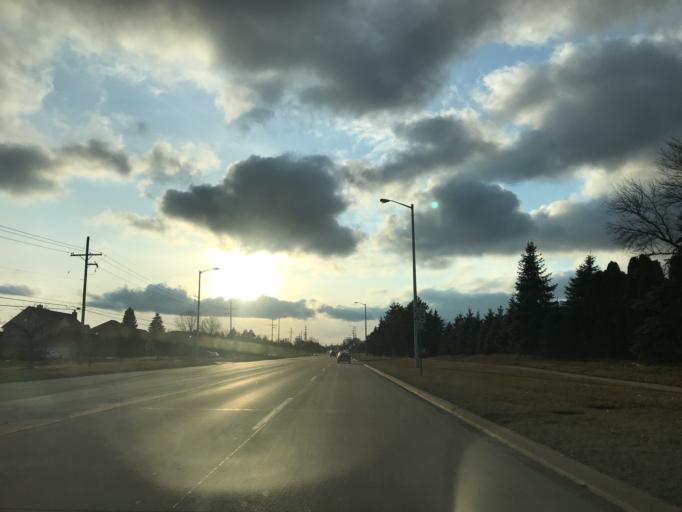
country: US
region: Michigan
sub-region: Oakland County
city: Farmington
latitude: 42.4255
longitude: -83.4087
